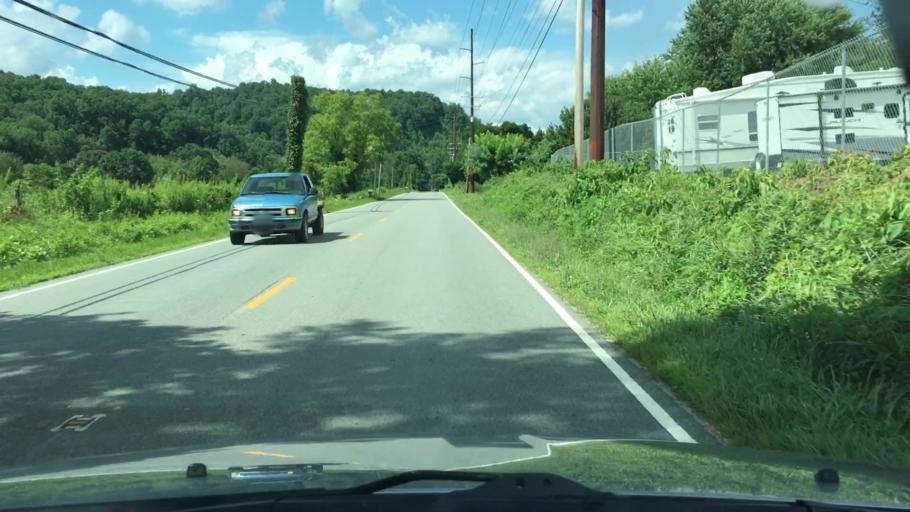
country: US
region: North Carolina
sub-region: Yancey County
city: Burnsville
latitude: 35.8911
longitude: -82.2149
